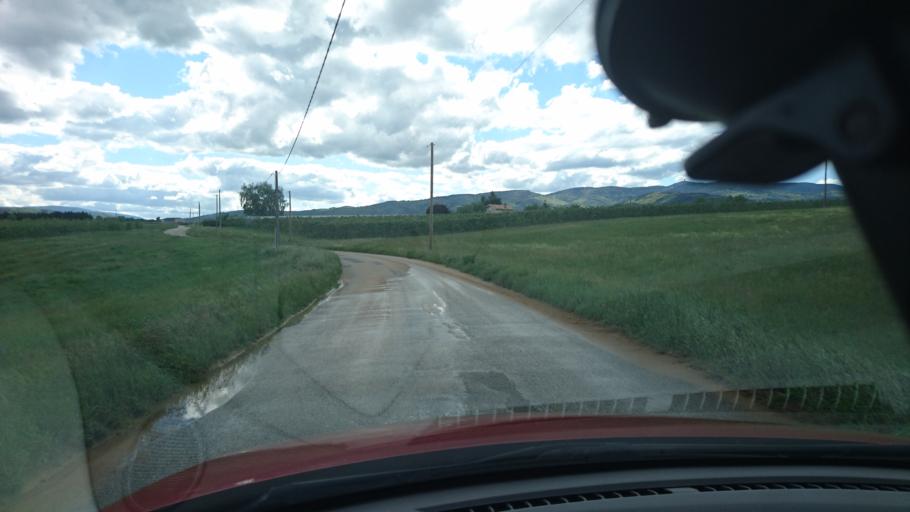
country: FR
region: Rhone-Alpes
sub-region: Departement de la Loire
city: Maclas
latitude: 45.3631
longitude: 4.7181
